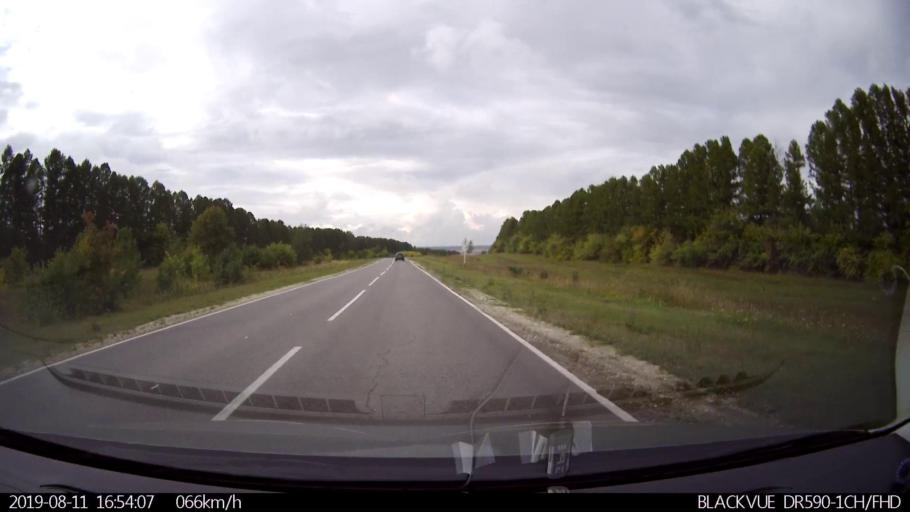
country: RU
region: Ulyanovsk
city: Mayna
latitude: 54.2696
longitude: 47.6672
